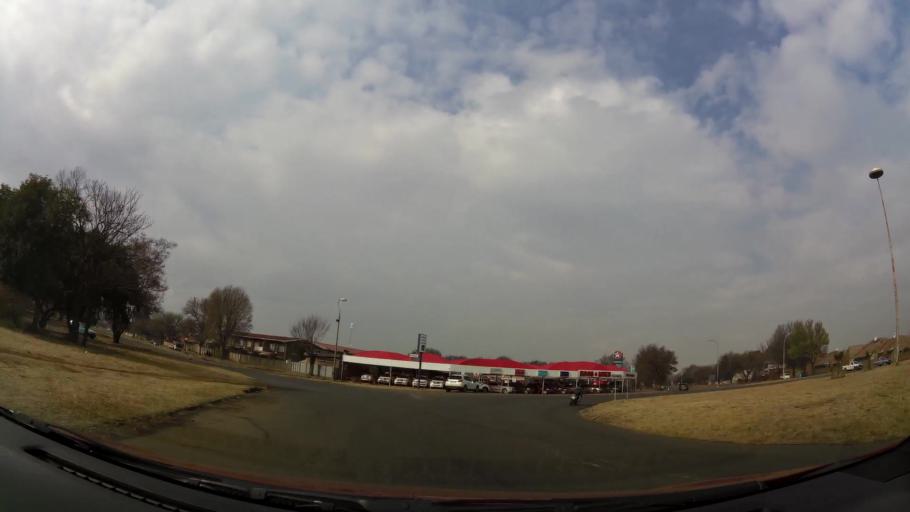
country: ZA
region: Gauteng
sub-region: Sedibeng District Municipality
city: Vanderbijlpark
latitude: -26.6835
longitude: 27.8349
